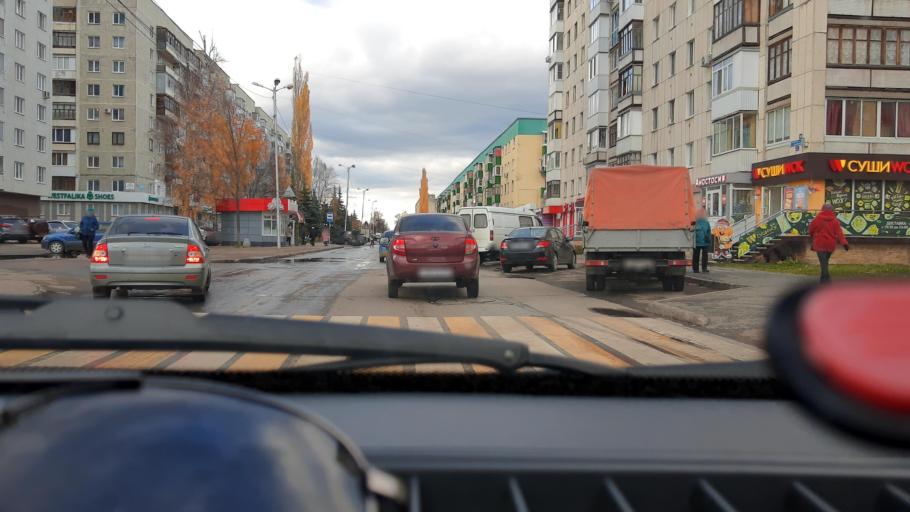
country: RU
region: Bashkortostan
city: Mikhaylovka
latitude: 54.7043
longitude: 55.8297
